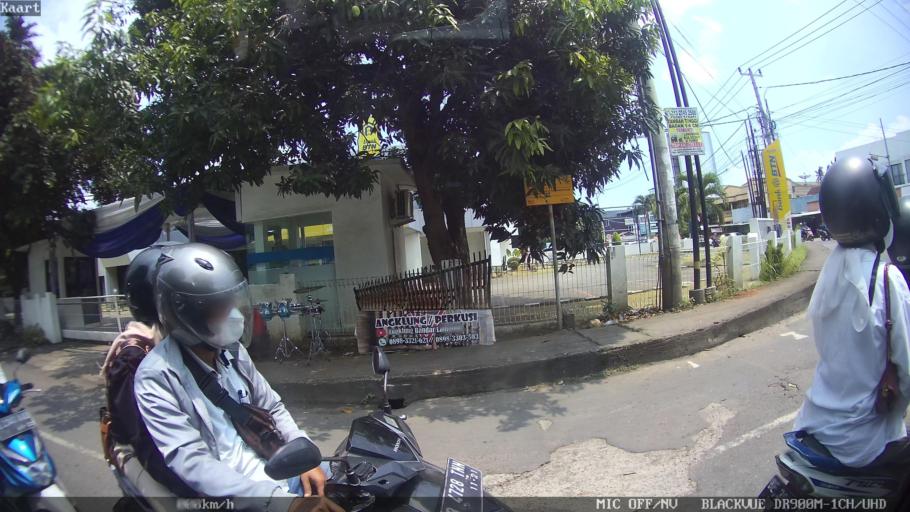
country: ID
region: Lampung
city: Kedaton
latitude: -5.3809
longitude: 105.2722
